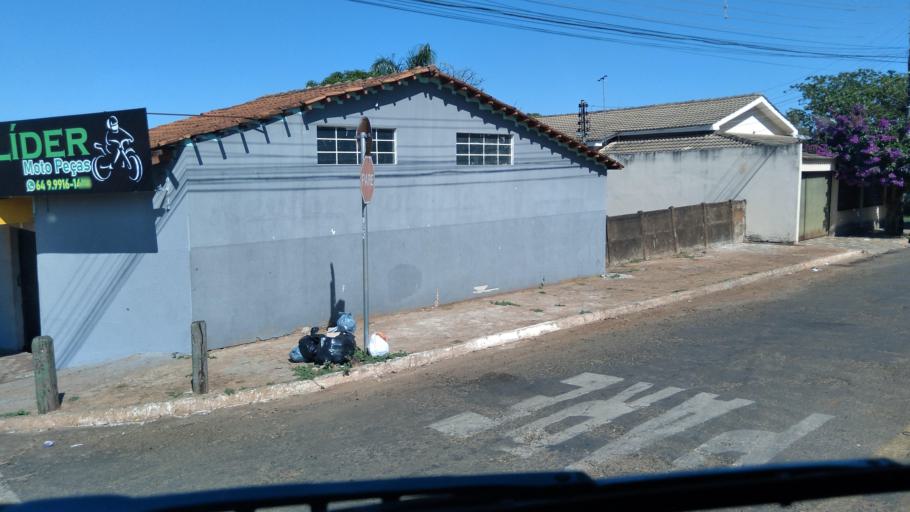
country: BR
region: Goias
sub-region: Mineiros
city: Mineiros
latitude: -17.5711
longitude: -52.5653
